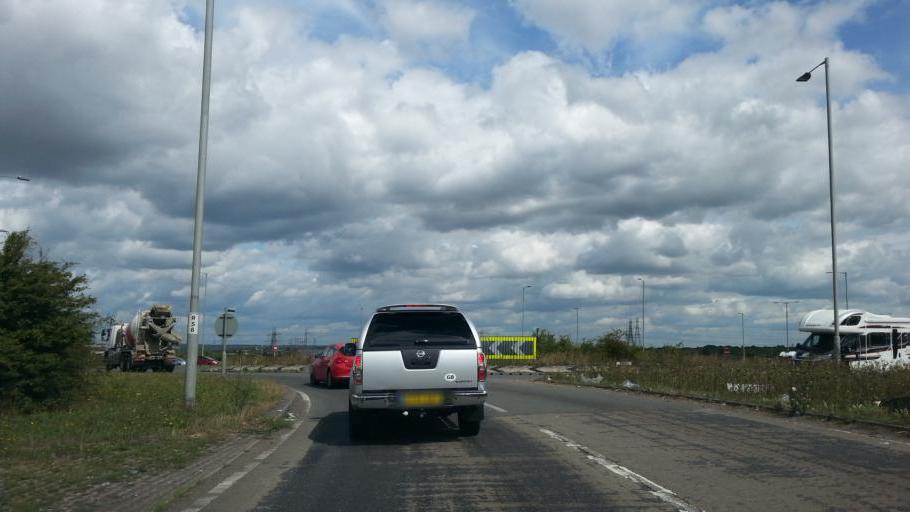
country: GB
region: England
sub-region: Essex
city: South Benfleet
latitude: 51.5829
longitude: 0.5609
